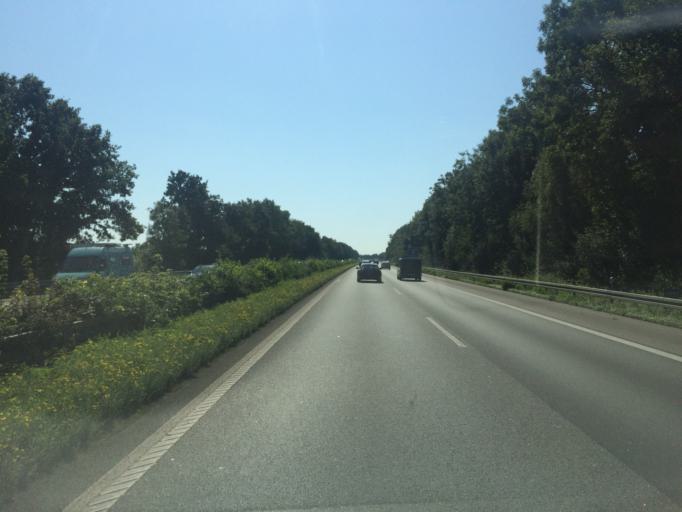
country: DE
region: North Rhine-Westphalia
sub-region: Regierungsbezirk Munster
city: Ascheberg
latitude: 51.7835
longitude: 7.6388
